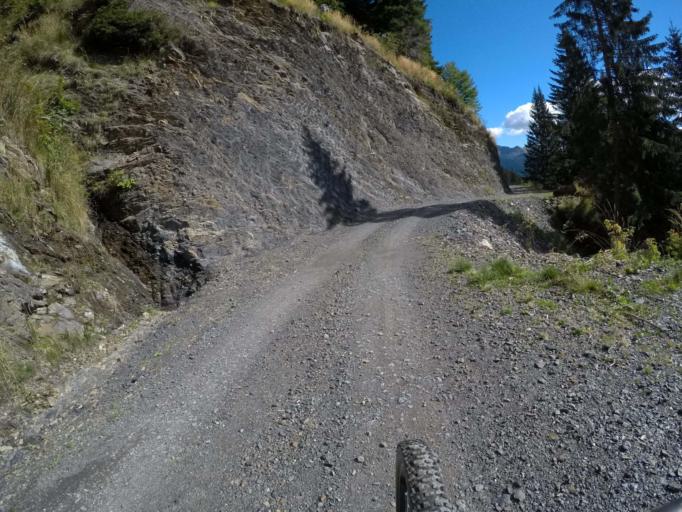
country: IT
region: Friuli Venezia Giulia
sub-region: Provincia di Udine
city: Ligosullo
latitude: 46.5670
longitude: 13.0868
